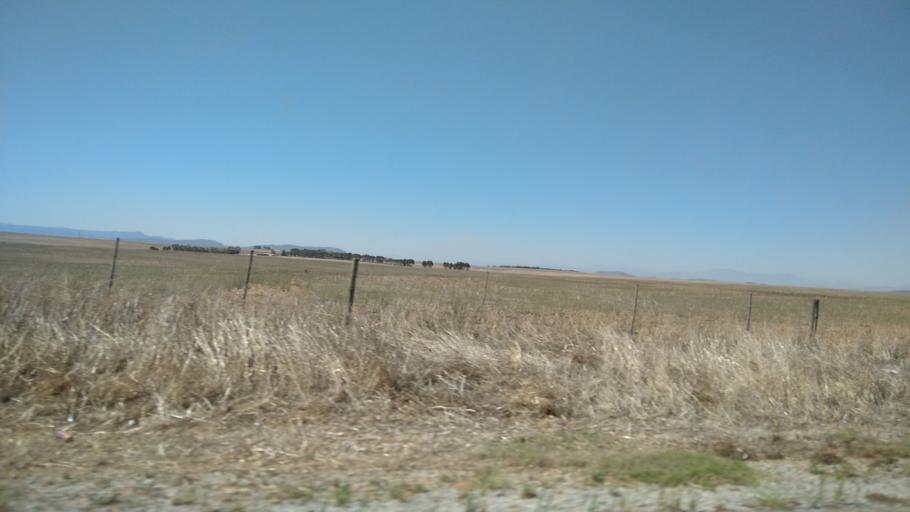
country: ZA
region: Western Cape
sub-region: West Coast District Municipality
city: Moorreesburg
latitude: -33.1768
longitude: 18.4885
